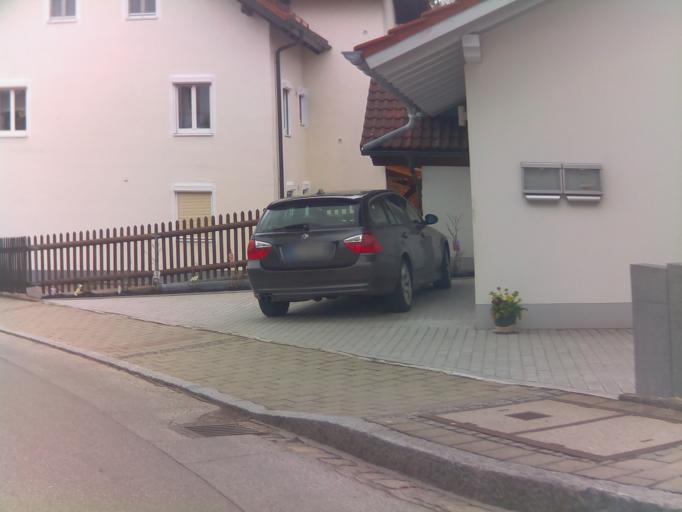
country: DE
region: Bavaria
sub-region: Upper Bavaria
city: Peissenberg
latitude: 47.7995
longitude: 11.0589
